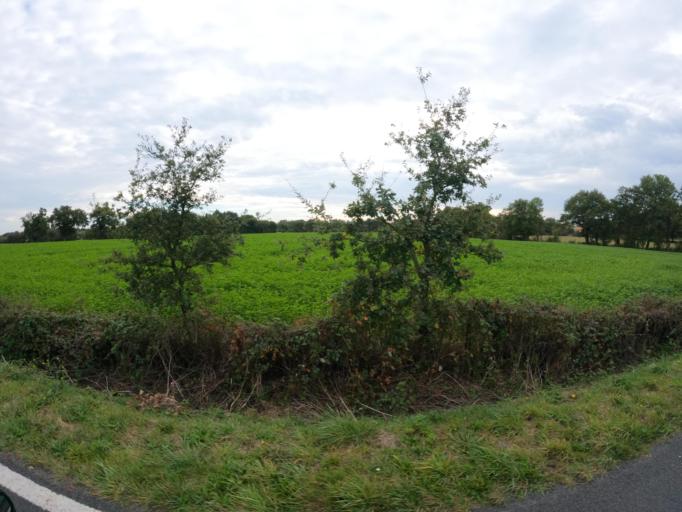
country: FR
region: Pays de la Loire
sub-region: Departement de la Loire-Atlantique
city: Boussay
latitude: 47.0538
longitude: -1.1670
